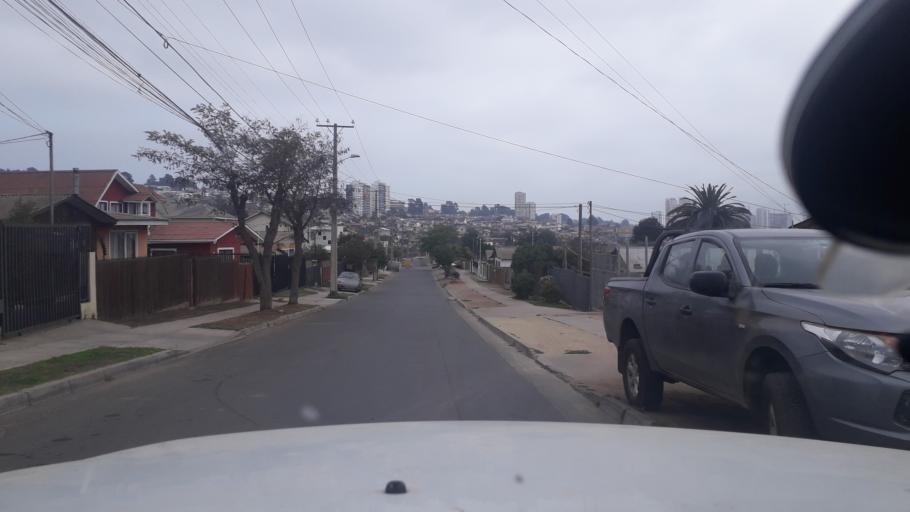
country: CL
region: Valparaiso
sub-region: Provincia de Valparaiso
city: Vina del Mar
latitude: -32.9345
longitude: -71.5226
